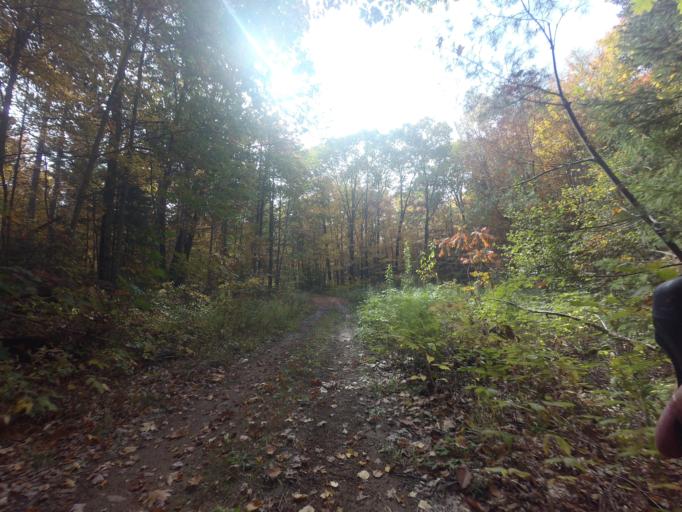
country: CA
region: Ontario
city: Pembroke
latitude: 45.7123
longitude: -77.2187
